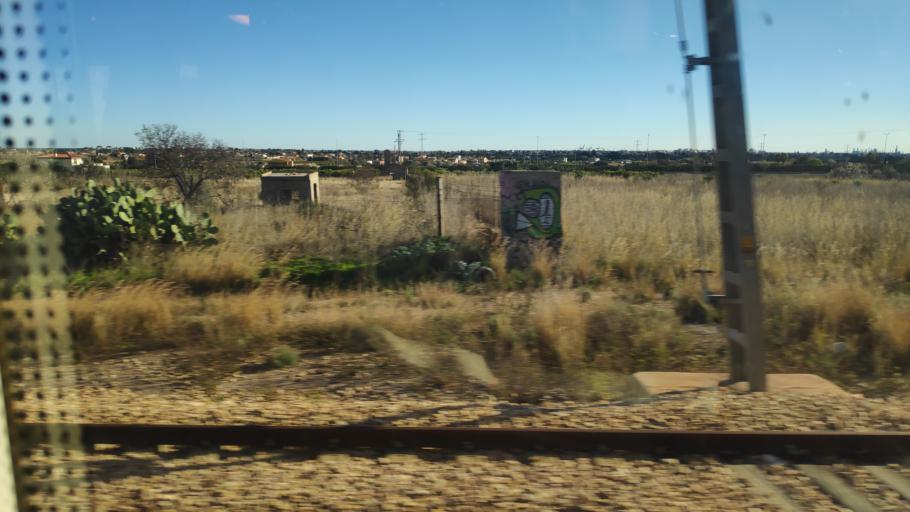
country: ES
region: Valencia
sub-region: Provincia de Castello
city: Castello de la Plana
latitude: 40.0259
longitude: 0.0046
